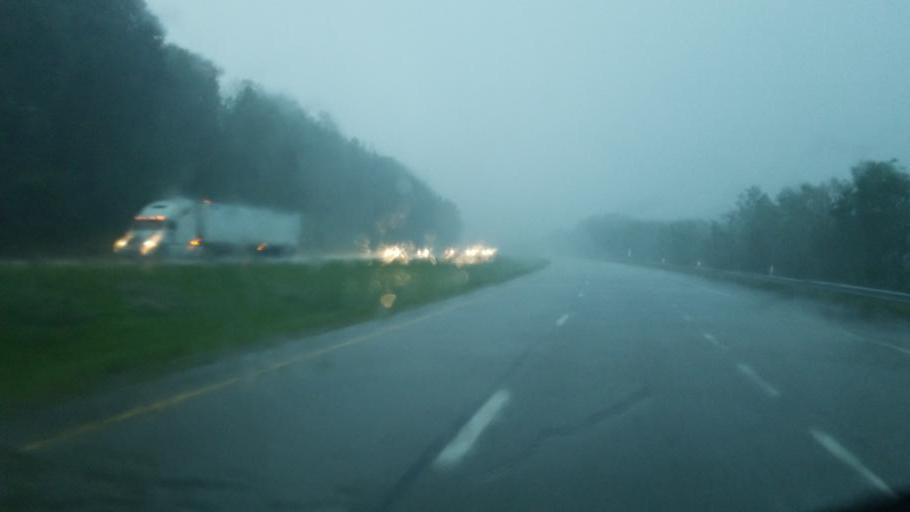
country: US
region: Pennsylvania
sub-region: Butler County
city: Prospect
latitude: 40.9184
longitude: -80.1332
